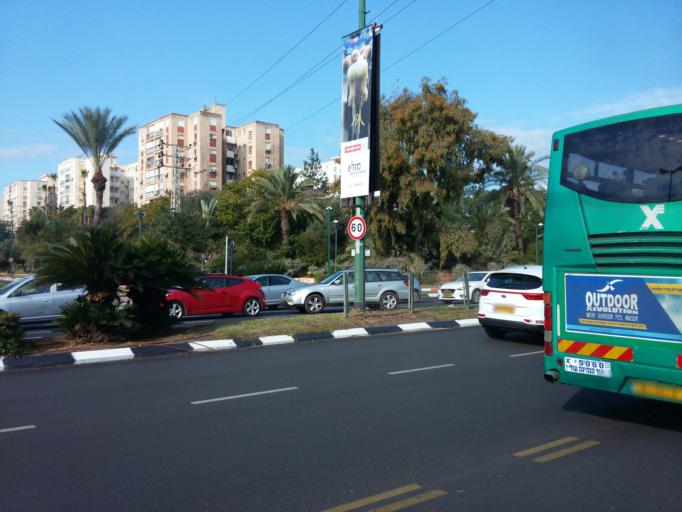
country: IL
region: Tel Aviv
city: Tel Aviv
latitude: 32.1032
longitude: 34.7926
